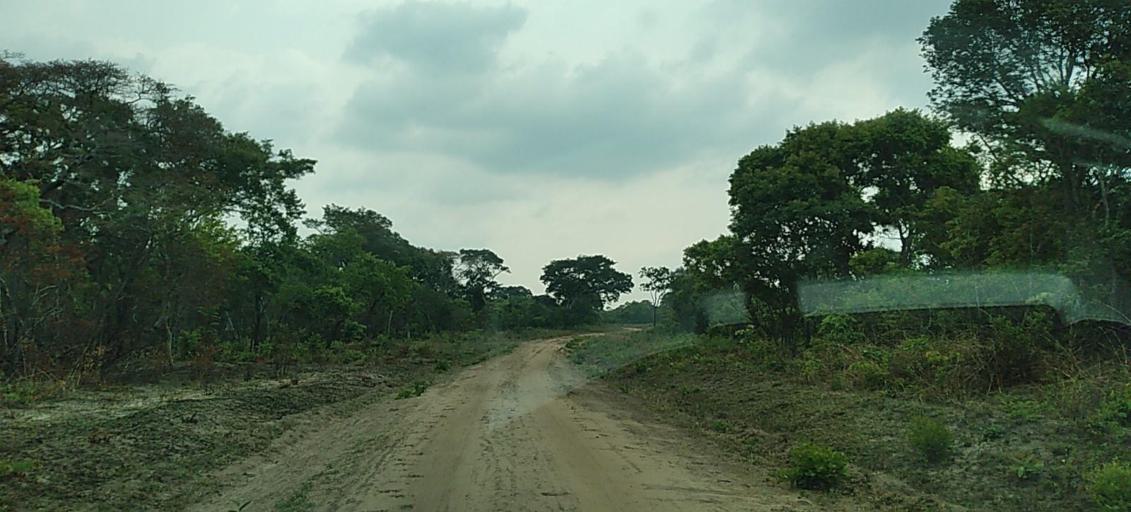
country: ZM
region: North-Western
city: Mwinilunga
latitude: -11.4143
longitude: 24.6104
